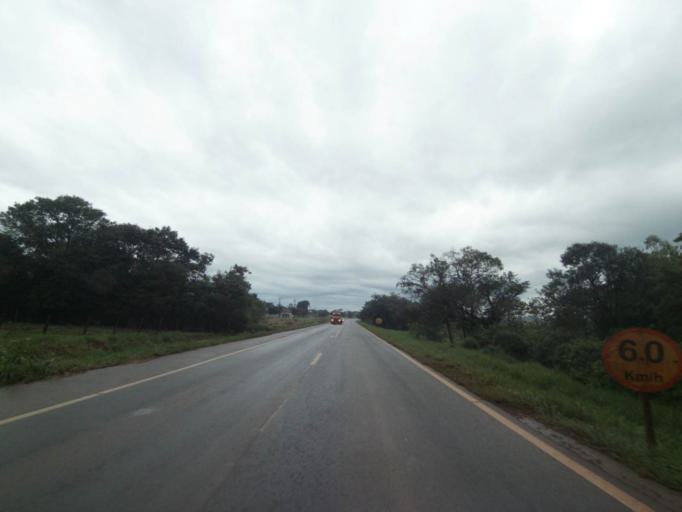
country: BR
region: Parana
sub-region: Toledo
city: Toledo
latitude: -24.6994
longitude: -53.7352
